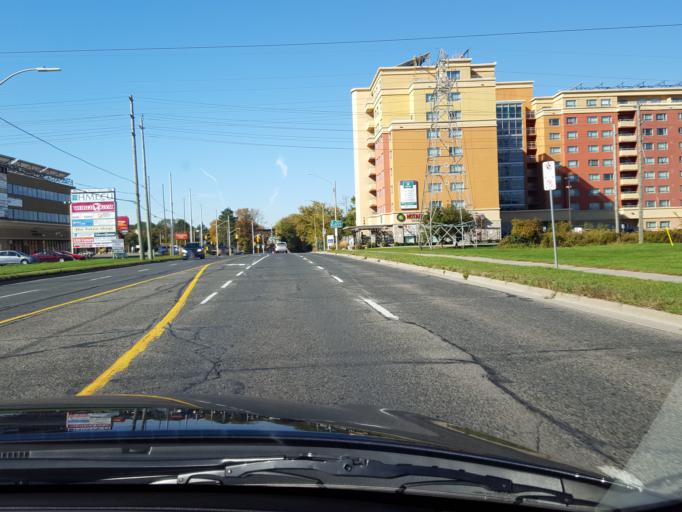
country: CA
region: Ontario
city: Ancaster
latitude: 43.2574
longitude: -79.9327
